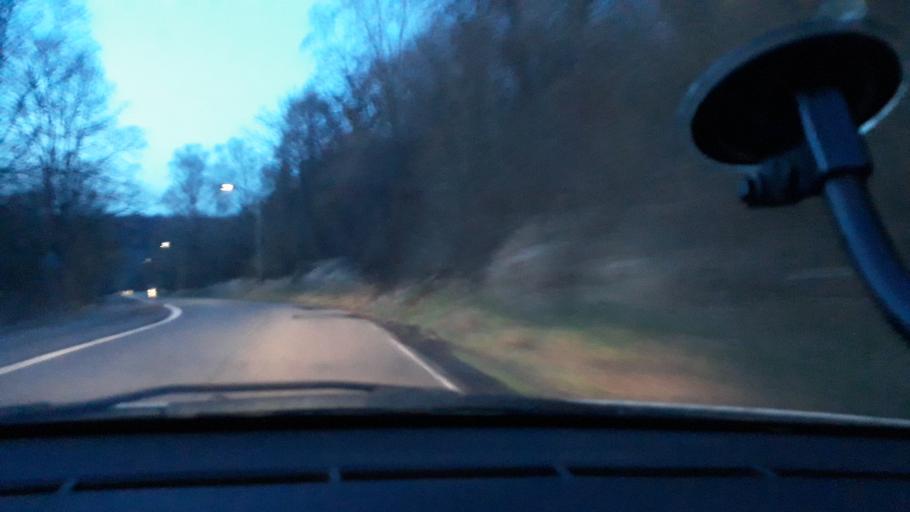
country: DE
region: Saarland
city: Blieskastel
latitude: 49.2071
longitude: 7.2191
